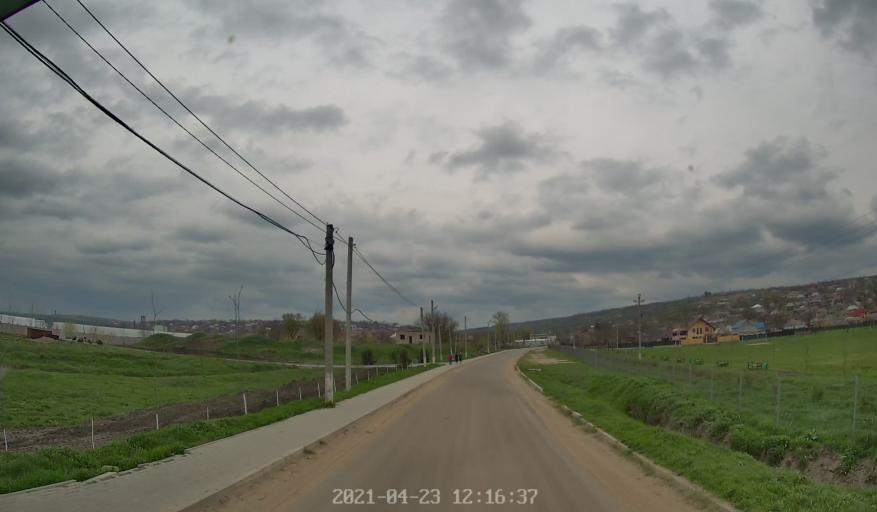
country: MD
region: Chisinau
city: Vadul lui Voda
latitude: 47.1209
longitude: 29.0018
